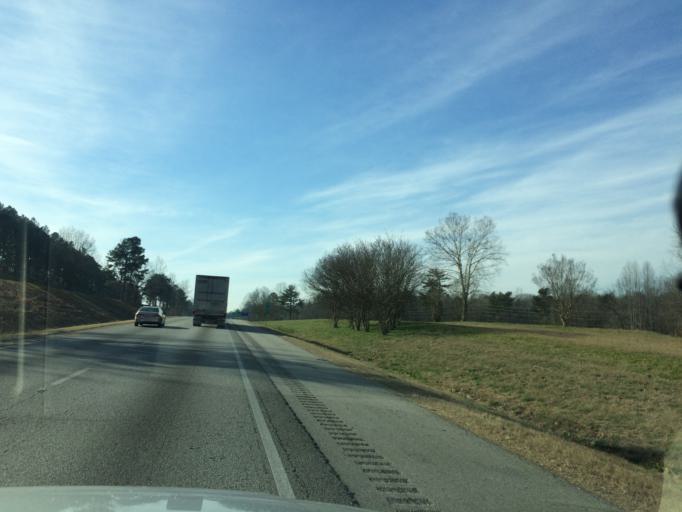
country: US
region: Georgia
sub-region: Franklin County
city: Gumlog
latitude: 34.4783
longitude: -83.0408
